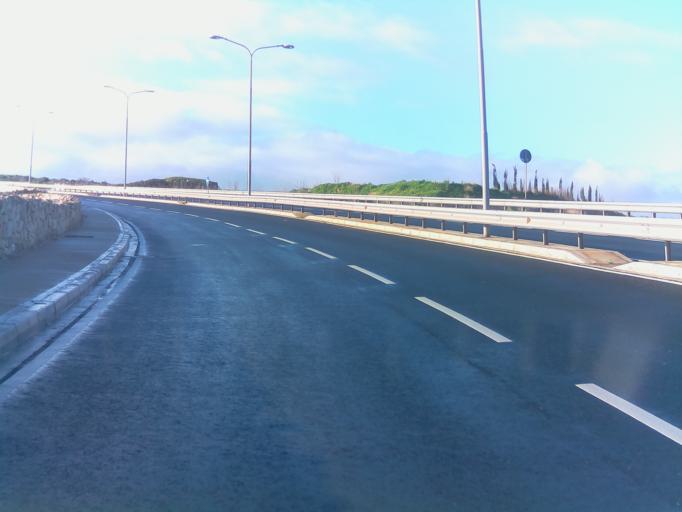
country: MT
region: Il-Mellieha
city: Mellieha
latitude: 35.9613
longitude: 14.3512
